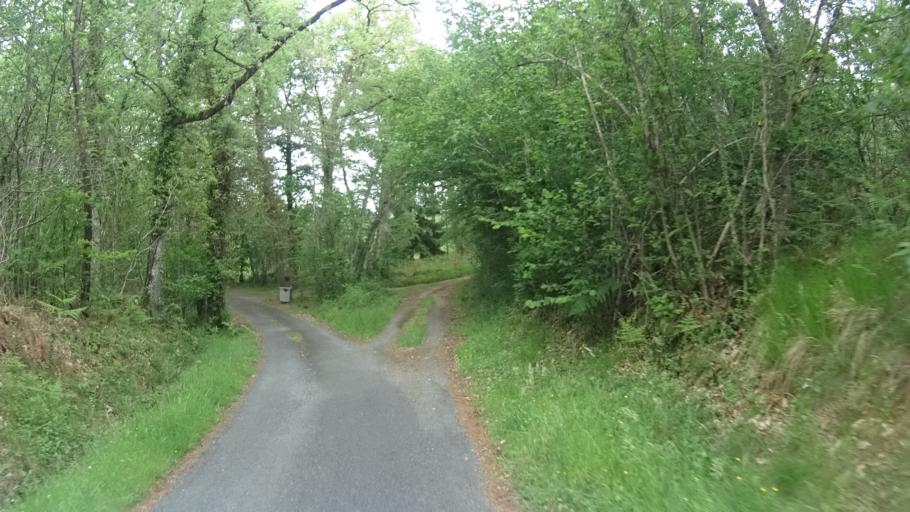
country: FR
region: Aquitaine
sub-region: Departement de la Dordogne
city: Lembras
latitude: 44.9708
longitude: 0.5049
